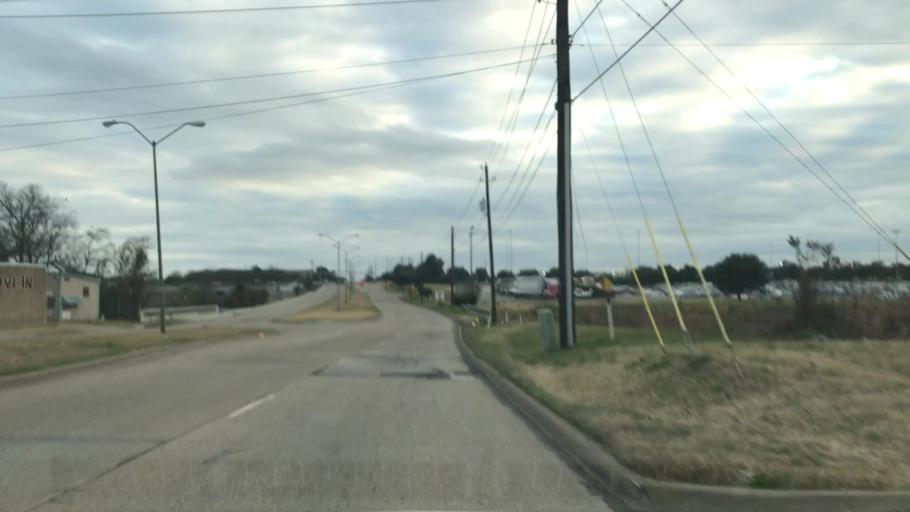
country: US
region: Texas
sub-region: Dallas County
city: Cockrell Hill
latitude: 32.7097
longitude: -96.9087
